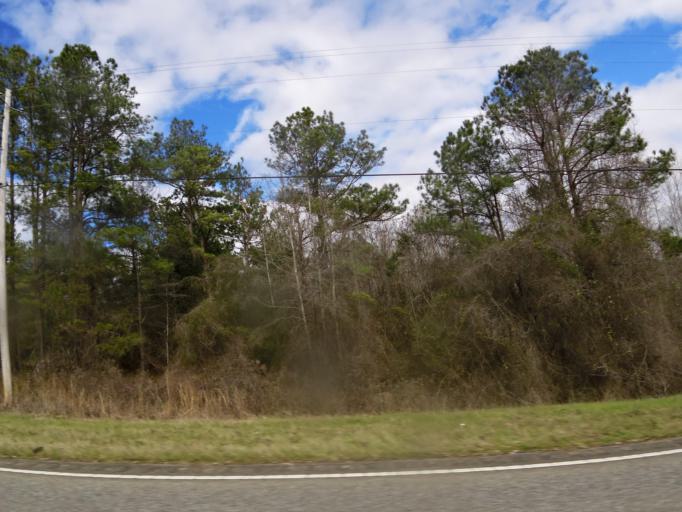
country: US
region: Alabama
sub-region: Barbour County
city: Eufaula
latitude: 32.0051
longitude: -85.2895
